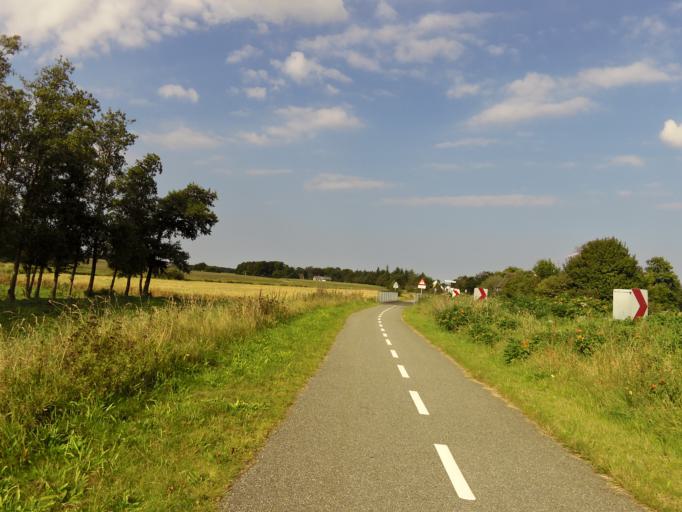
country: DK
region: South Denmark
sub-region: Vejen Kommune
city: Vejen
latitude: 55.4427
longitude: 9.1363
